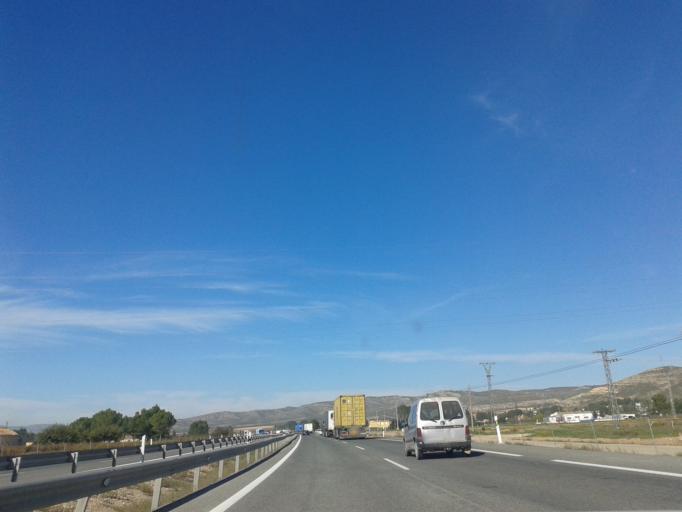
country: ES
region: Valencia
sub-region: Provincia de Alicante
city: Villena
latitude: 38.6622
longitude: -0.8793
